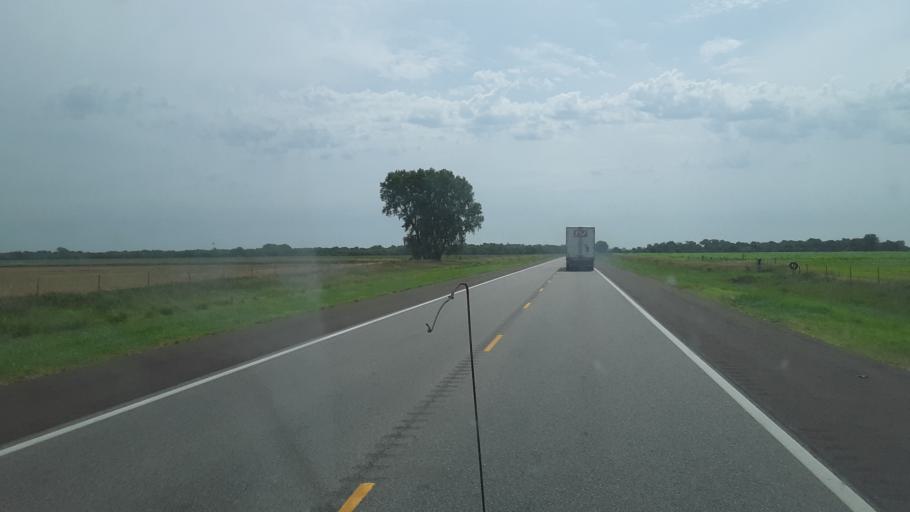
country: US
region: Kansas
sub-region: Reno County
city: Nickerson
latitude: 37.9850
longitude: -98.1530
